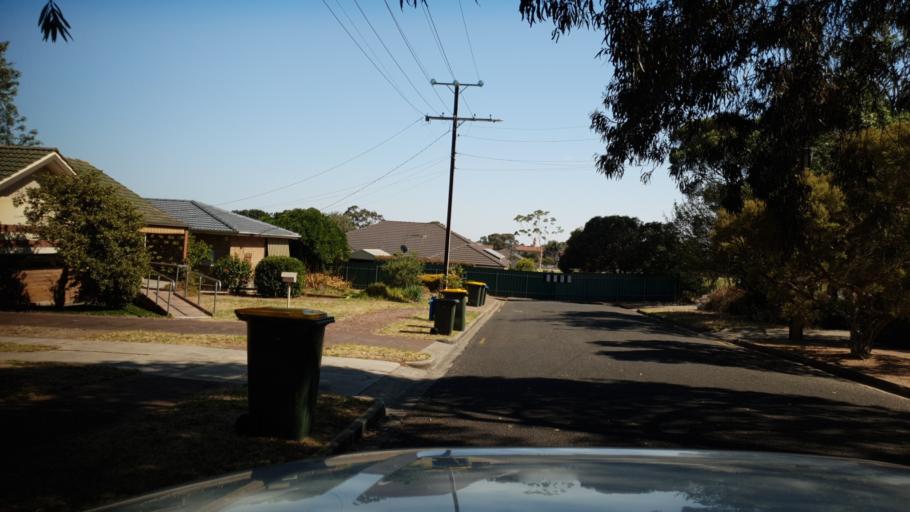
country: AU
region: South Australia
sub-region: Mitcham
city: Clapham
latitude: -34.9948
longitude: 138.5891
